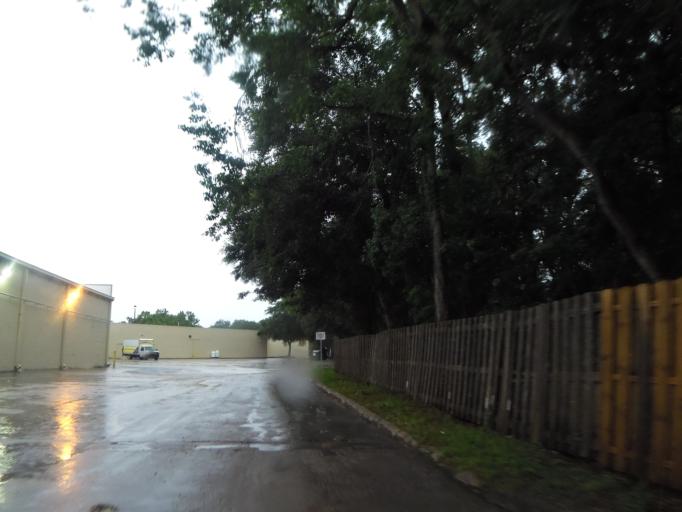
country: US
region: Florida
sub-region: Duval County
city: Jacksonville
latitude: 30.2887
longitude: -81.5648
